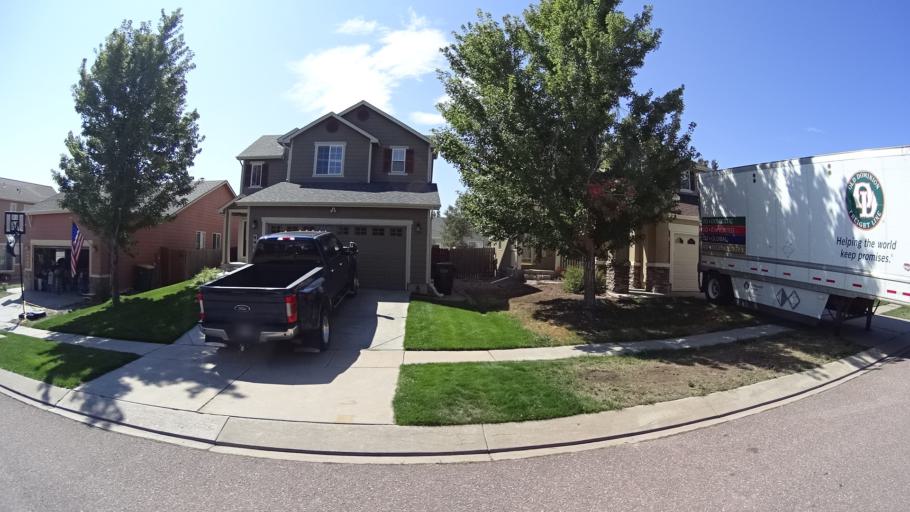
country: US
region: Colorado
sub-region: El Paso County
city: Cimarron Hills
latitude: 38.9185
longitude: -104.7025
